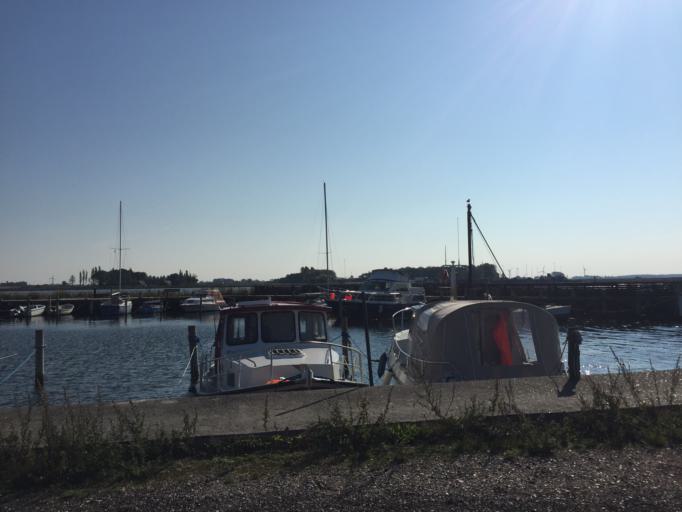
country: DK
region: Zealand
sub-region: Lolland Kommune
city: Nakskov
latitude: 54.8776
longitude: 11.0235
